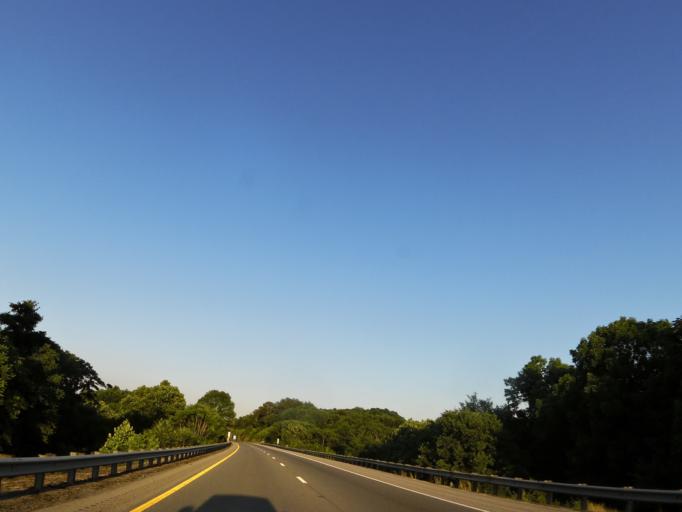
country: US
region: Tennessee
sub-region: Smith County
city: Gordonsville
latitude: 36.1423
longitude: -85.8440
